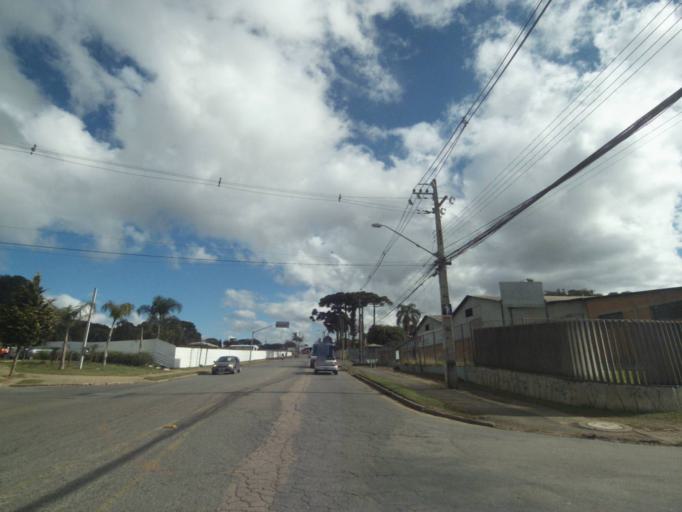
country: BR
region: Parana
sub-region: Sao Jose Dos Pinhais
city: Sao Jose dos Pinhais
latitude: -25.5300
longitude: -49.2946
